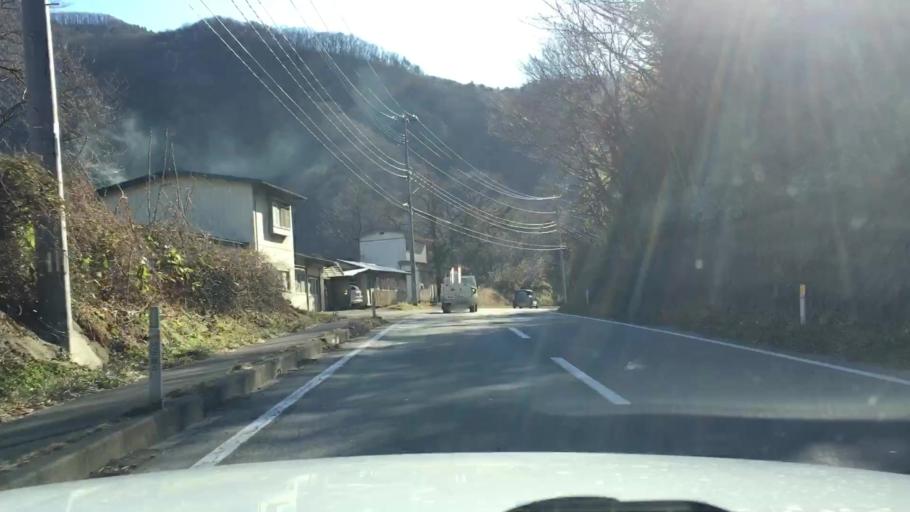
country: JP
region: Iwate
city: Miyako
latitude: 39.6214
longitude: 141.8109
